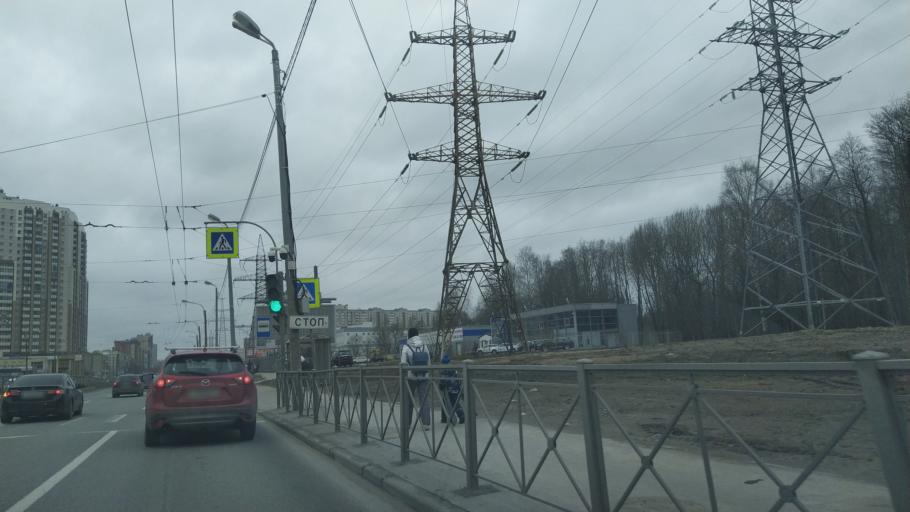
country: RU
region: Leningrad
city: Chernaya Rechka
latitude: 60.0018
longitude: 30.3078
